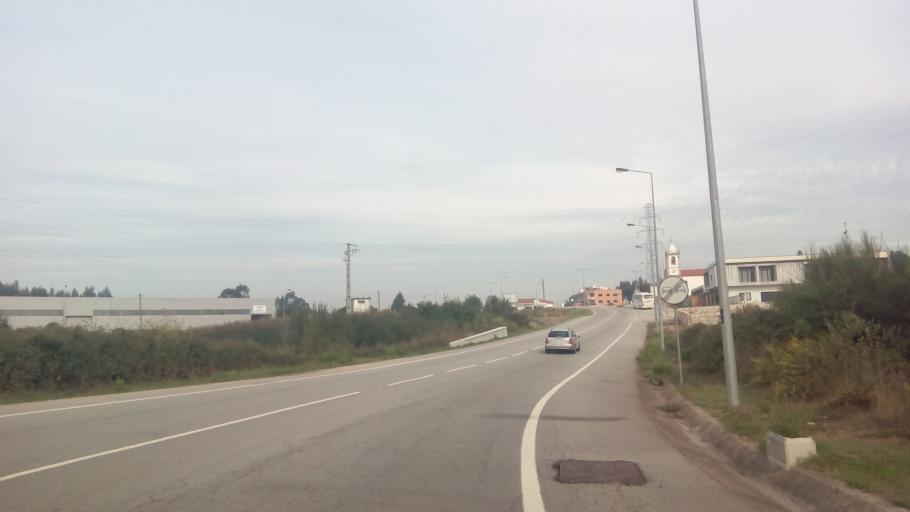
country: PT
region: Porto
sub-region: Paredes
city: Gandra
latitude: 41.1990
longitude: -8.4384
